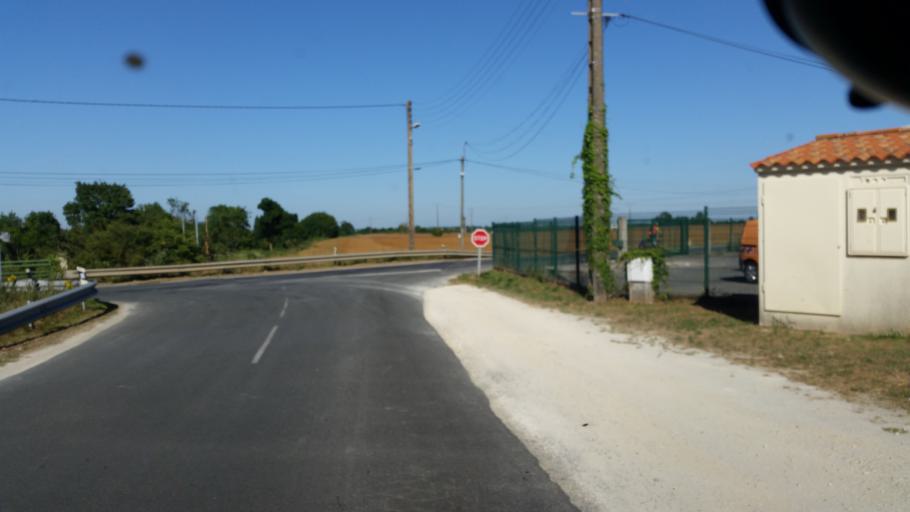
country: FR
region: Poitou-Charentes
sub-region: Departement de la Charente-Maritime
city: Marans
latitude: 46.3021
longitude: -0.9839
